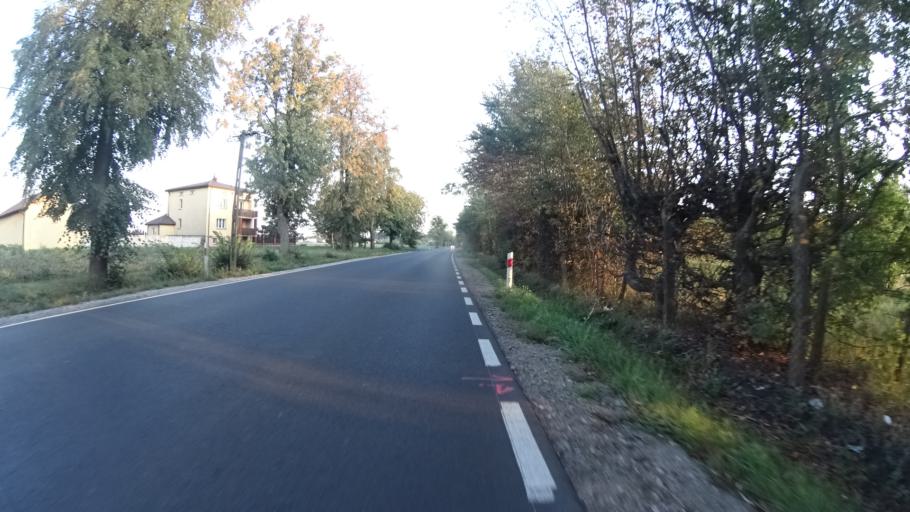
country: PL
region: Masovian Voivodeship
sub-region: Powiat warszawski zachodni
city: Ozarow Mazowiecki
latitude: 52.2290
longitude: 20.7717
